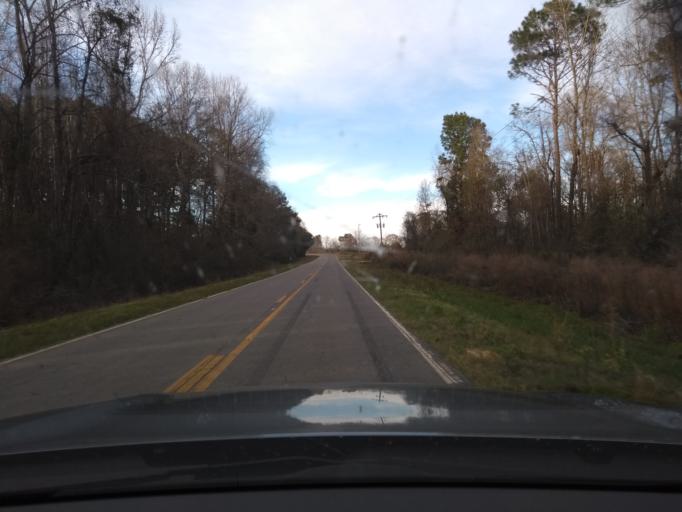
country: US
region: Georgia
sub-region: Evans County
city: Claxton
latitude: 32.2380
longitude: -81.7701
